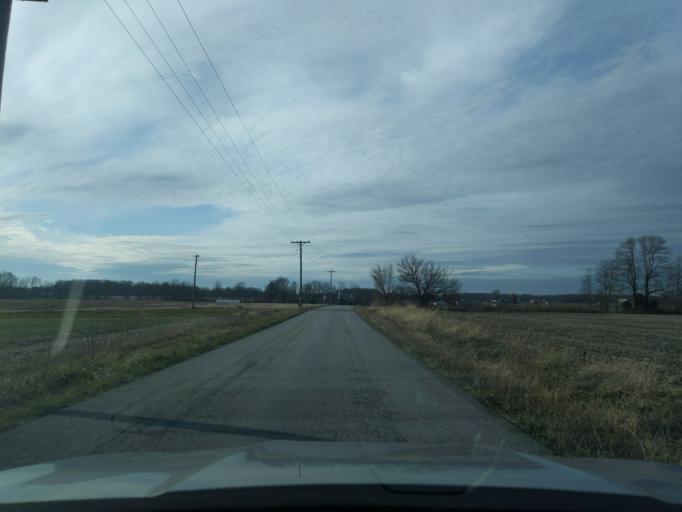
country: US
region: Indiana
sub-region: Decatur County
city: Greensburg
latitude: 39.2149
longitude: -85.4515
